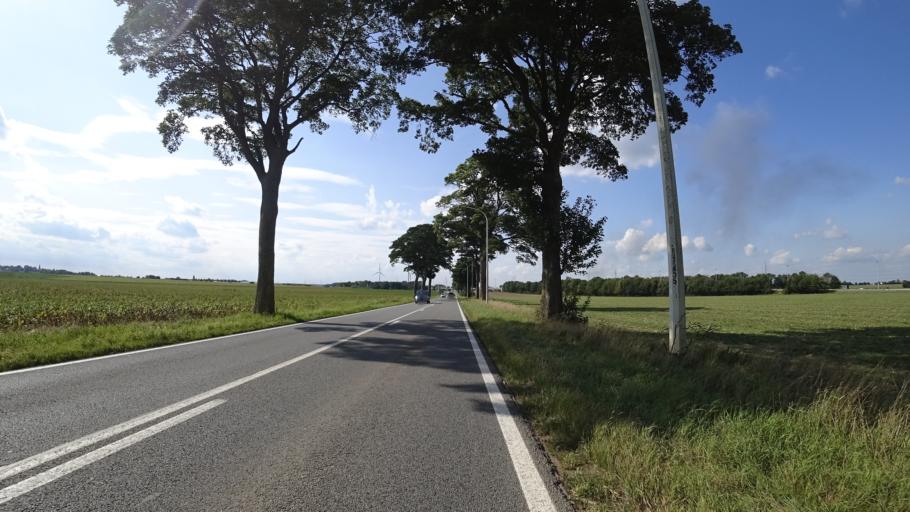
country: BE
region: Wallonia
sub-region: Province de Namur
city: Floreffe
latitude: 50.4930
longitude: 4.7359
